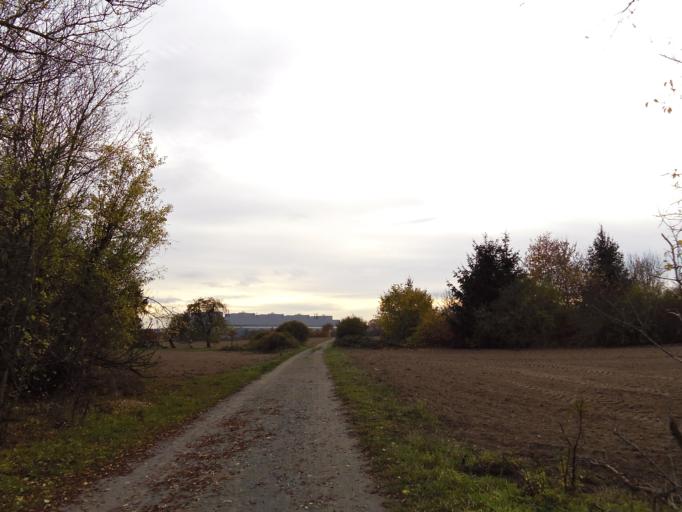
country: DE
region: Hesse
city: Morfelden-Walldorf
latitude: 49.9925
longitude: 8.5853
